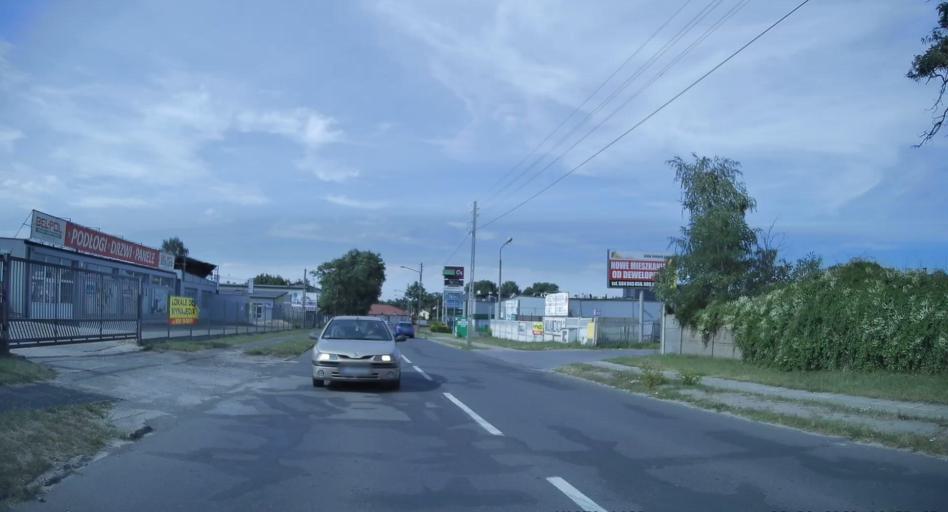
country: PL
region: Lodz Voivodeship
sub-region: Powiat tomaszowski
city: Tomaszow Mazowiecki
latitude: 51.5329
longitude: 19.9966
